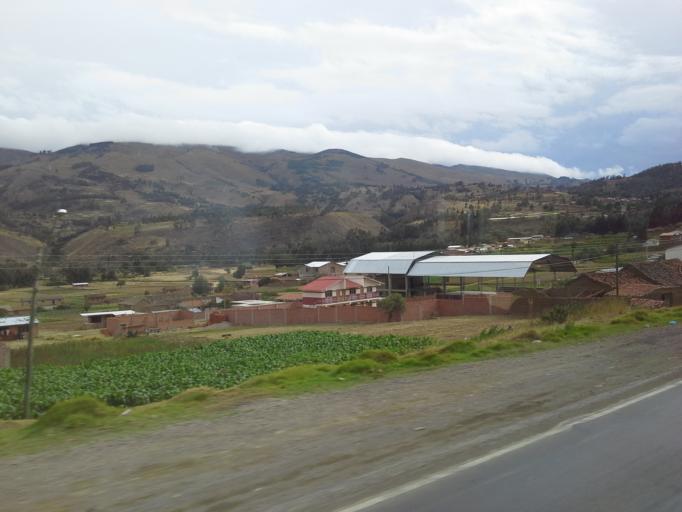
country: BO
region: Cochabamba
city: Colomi
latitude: -17.4197
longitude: -65.9526
